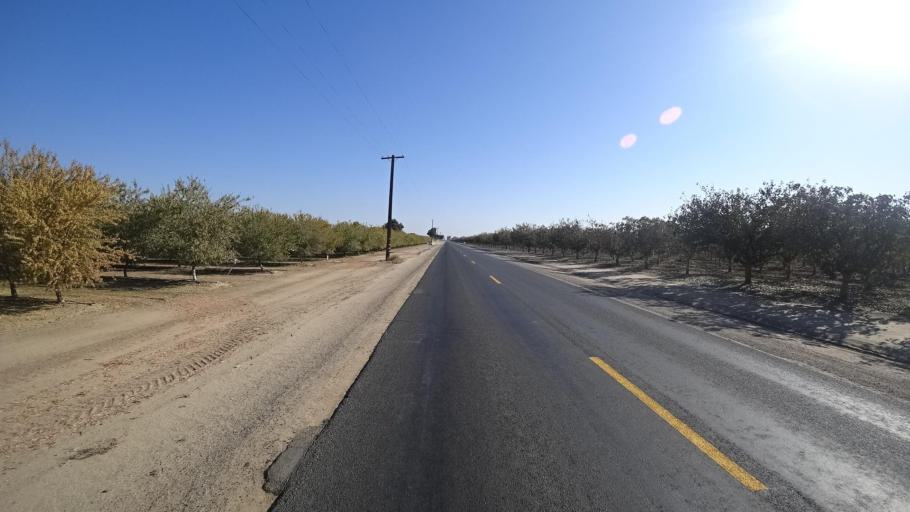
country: US
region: California
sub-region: Kern County
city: Delano
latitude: 35.7177
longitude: -119.3468
